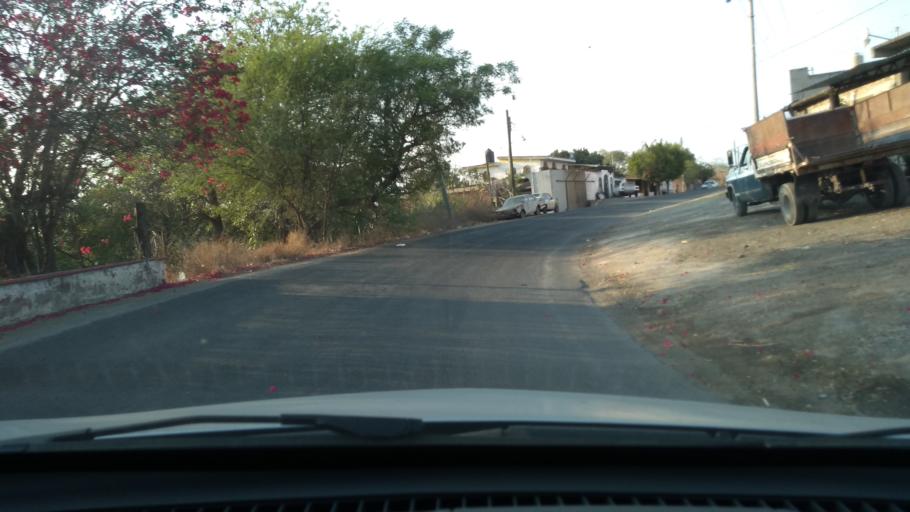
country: MX
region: Morelos
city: Puente de Ixtla
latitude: 18.6078
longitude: -99.3179
